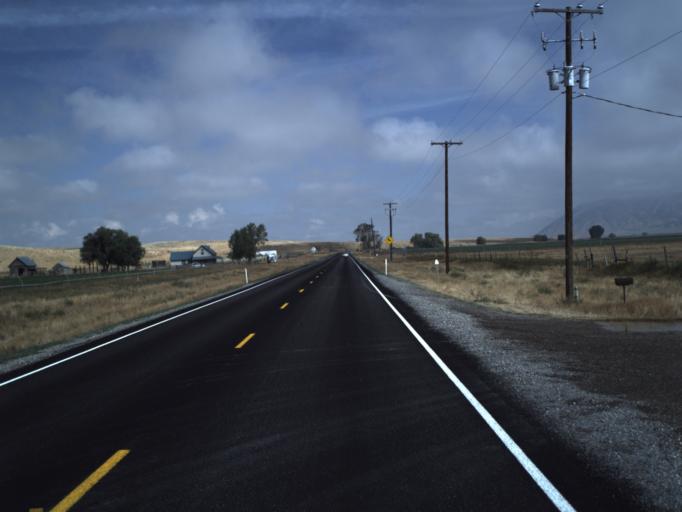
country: US
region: Utah
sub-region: Rich County
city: Randolph
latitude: 41.5302
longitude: -111.1629
